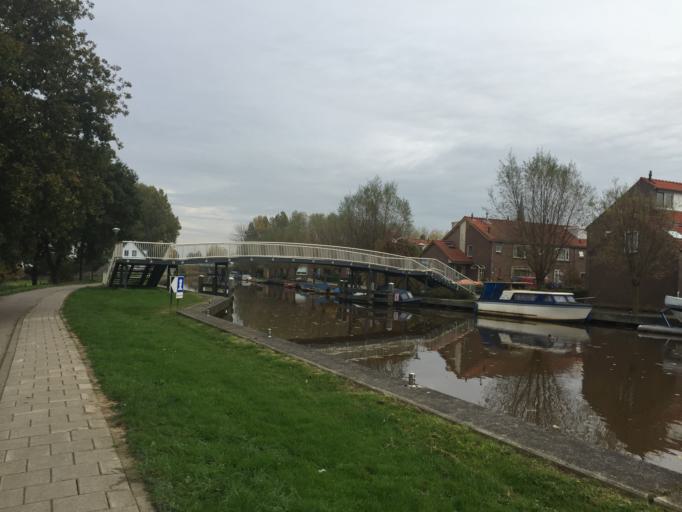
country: NL
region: Utrecht
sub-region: Gemeente De Ronde Venen
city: Mijdrecht
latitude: 52.1972
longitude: 4.9021
